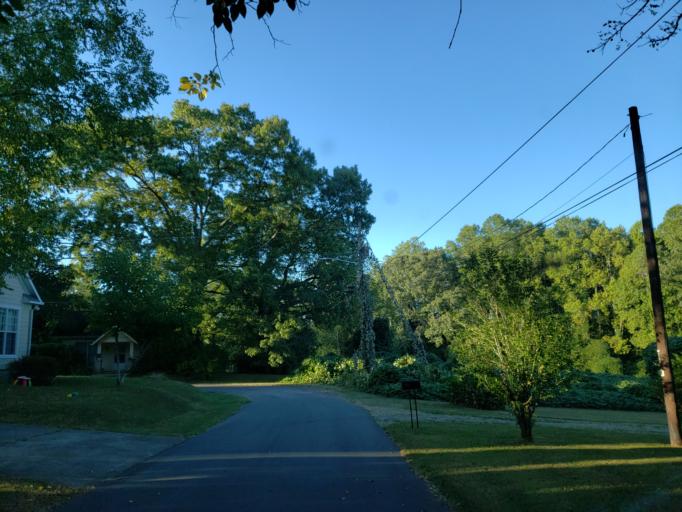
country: US
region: Georgia
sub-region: Pickens County
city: Jasper
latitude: 34.4649
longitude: -84.4276
